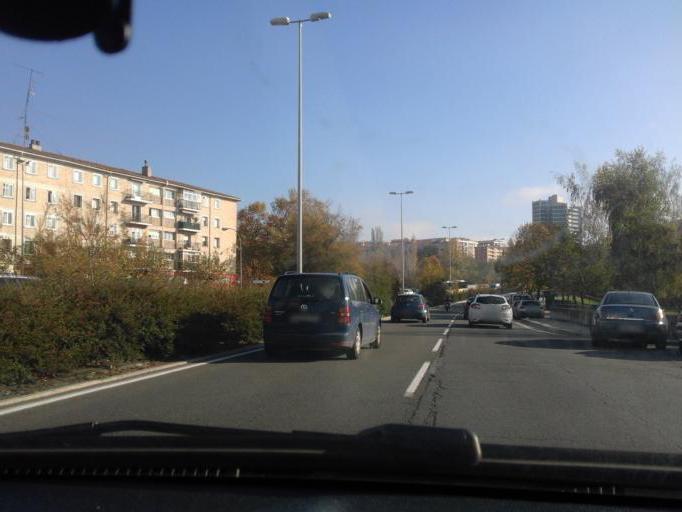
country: ES
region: Navarre
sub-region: Provincia de Navarra
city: Ermitagana
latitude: 42.8196
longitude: -1.6688
